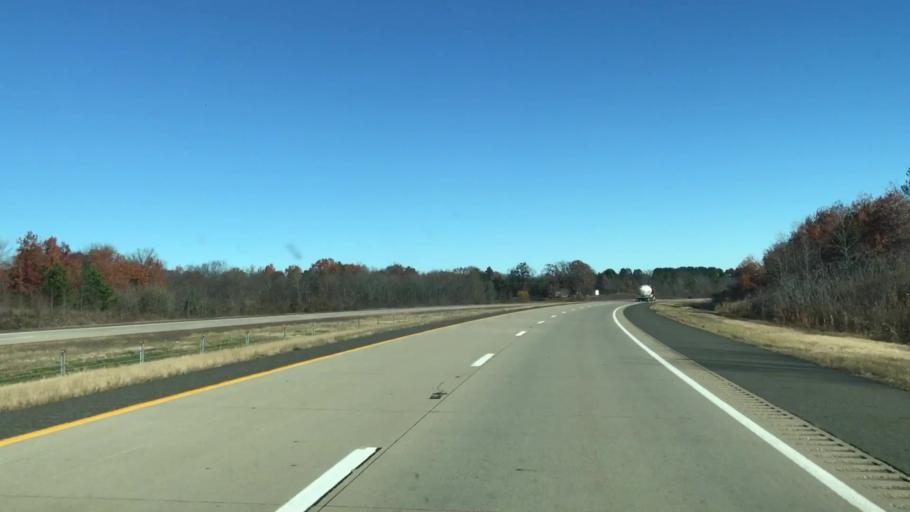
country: US
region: Texas
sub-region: Cass County
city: Queen City
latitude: 33.1555
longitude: -93.8895
